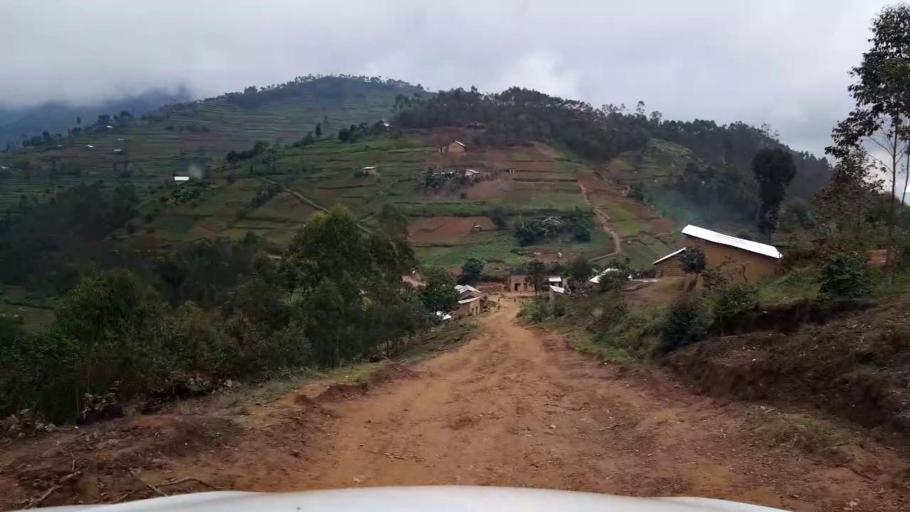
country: RW
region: Northern Province
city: Musanze
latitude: -1.5970
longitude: 29.7768
